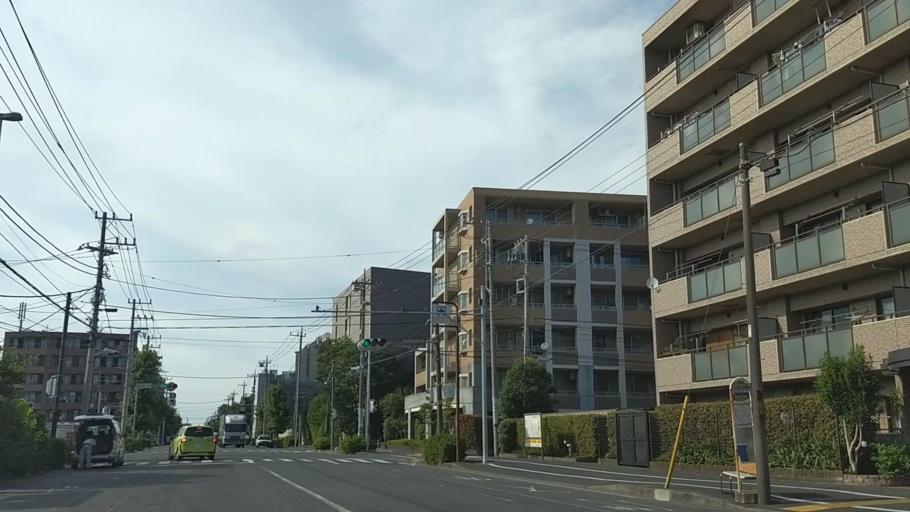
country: JP
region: Kanagawa
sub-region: Kawasaki-shi
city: Kawasaki
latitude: 35.5046
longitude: 139.6936
